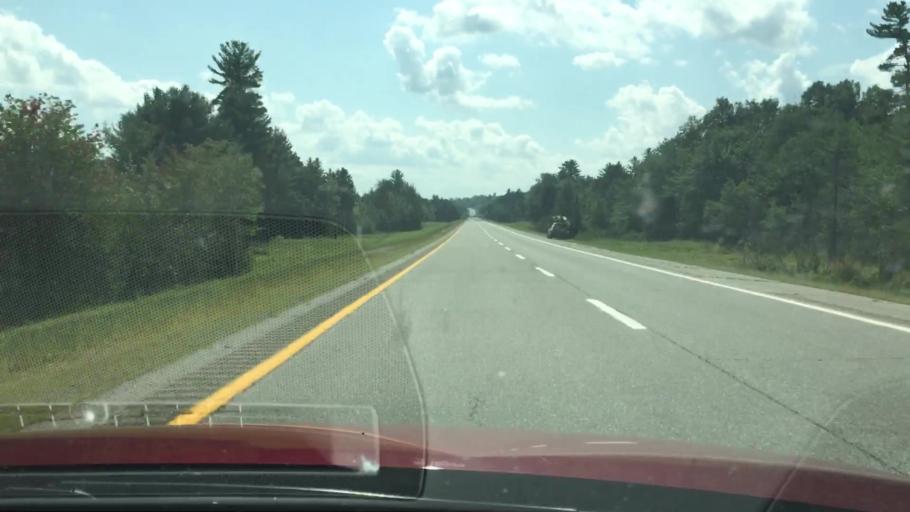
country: US
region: Maine
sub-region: Penobscot County
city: Lincoln
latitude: 45.4758
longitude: -68.5775
